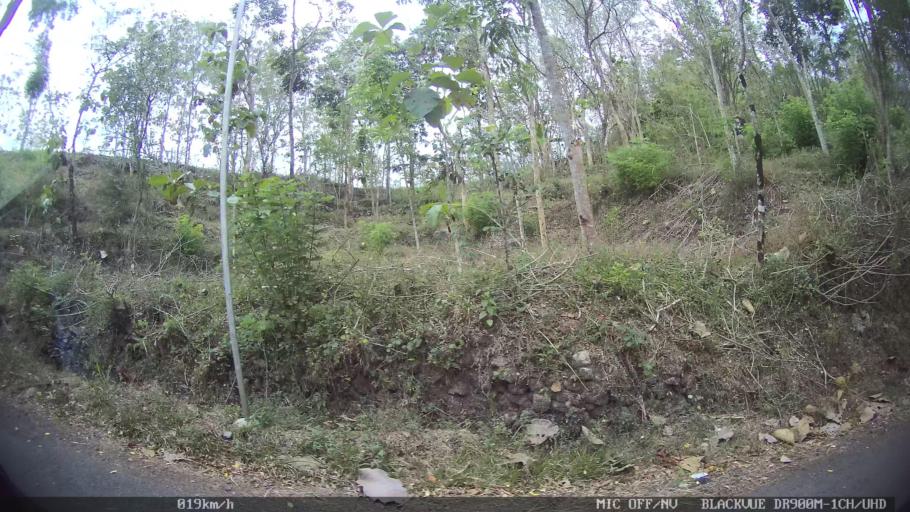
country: ID
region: Central Java
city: Candi Prambanan
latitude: -7.7983
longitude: 110.5213
